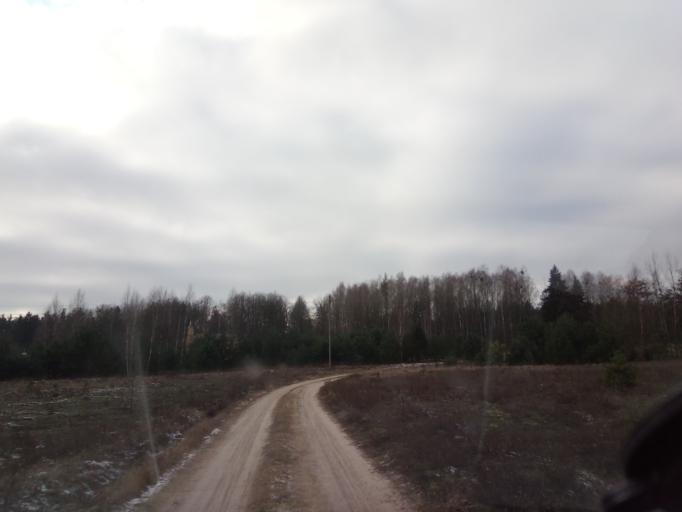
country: LT
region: Alytaus apskritis
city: Druskininkai
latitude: 53.9551
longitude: 24.2952
